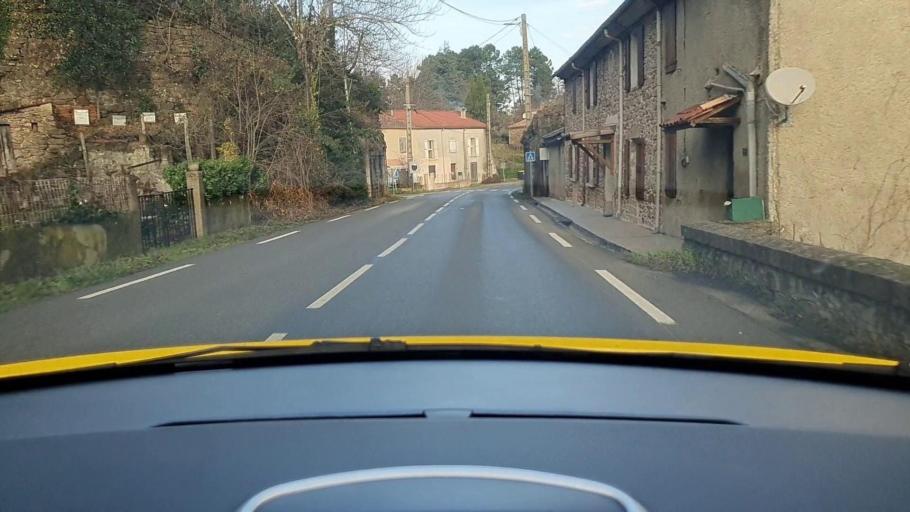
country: FR
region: Languedoc-Roussillon
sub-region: Departement du Gard
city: Branoux-les-Taillades
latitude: 44.2782
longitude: 4.0038
